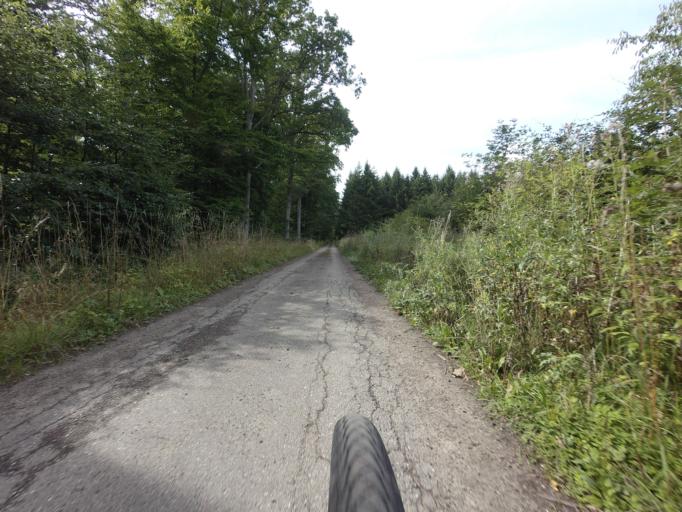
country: DK
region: Zealand
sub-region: Faxe Kommune
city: Fakse Ladeplads
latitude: 55.2341
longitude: 12.1967
